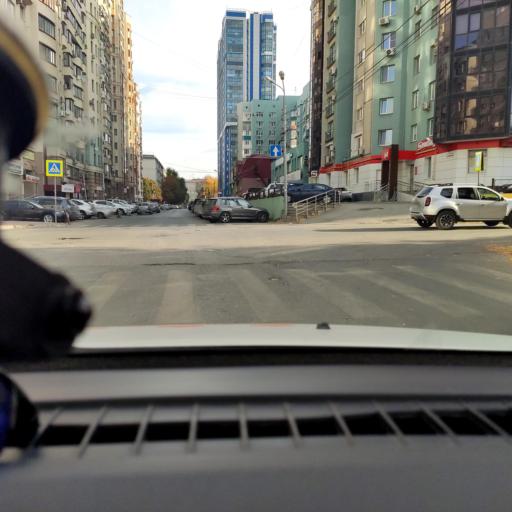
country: RU
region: Samara
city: Samara
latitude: 53.2026
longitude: 50.1212
